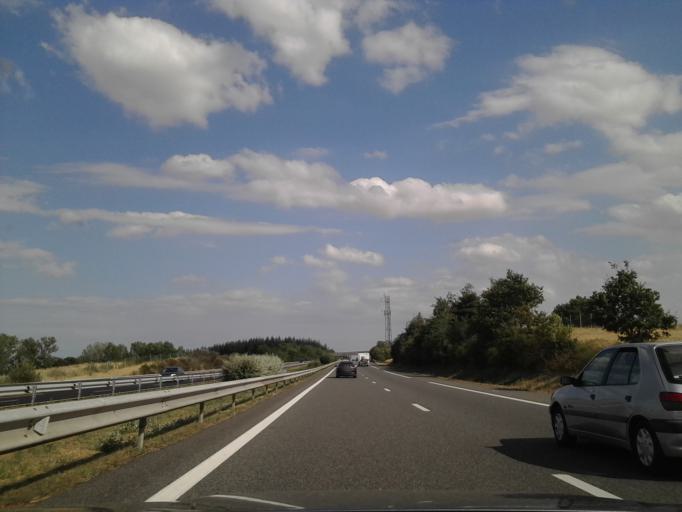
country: FR
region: Auvergne
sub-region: Departement de l'Allier
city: Bellenaves
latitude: 46.2576
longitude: 3.0749
